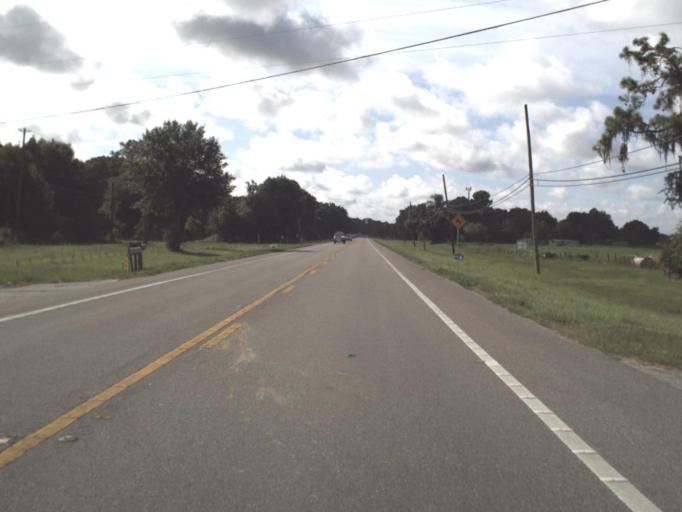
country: US
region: Florida
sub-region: Pasco County
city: Land O' Lakes
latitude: 28.3102
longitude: -82.5043
